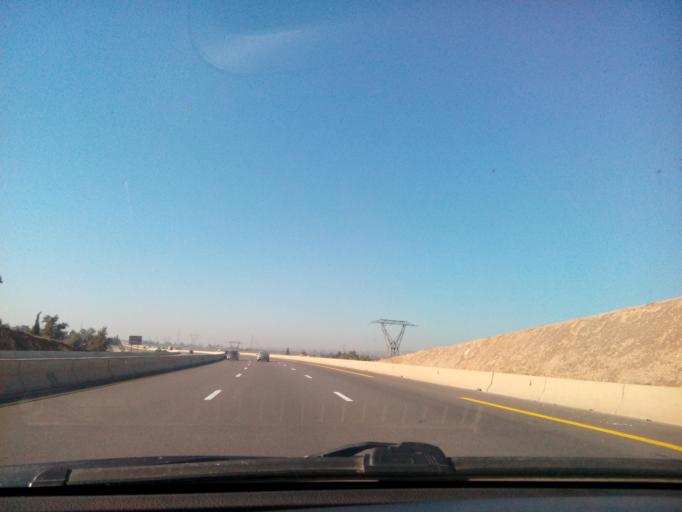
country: DZ
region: Chlef
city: Boukadir
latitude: 36.0498
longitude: 1.1130
